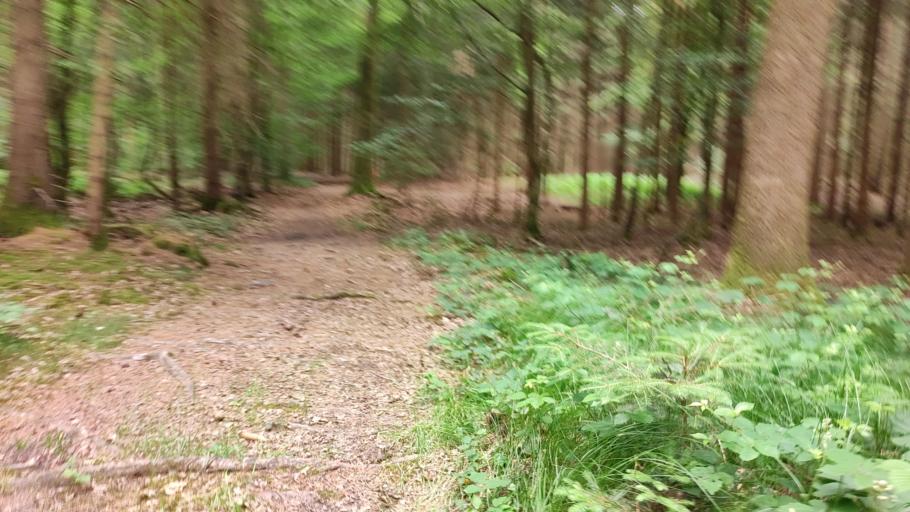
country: DE
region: Bavaria
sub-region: Swabia
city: Adelsried
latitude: 48.4118
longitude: 10.6983
